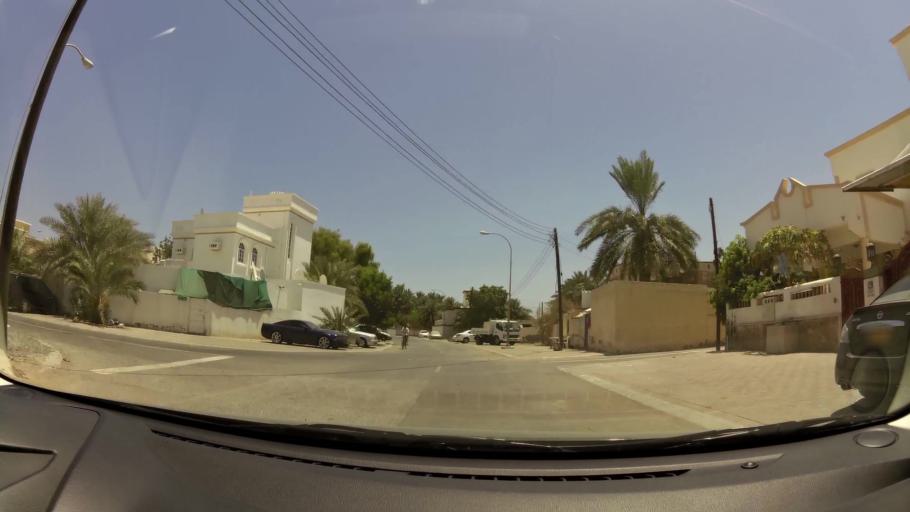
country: OM
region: Muhafazat Masqat
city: As Sib al Jadidah
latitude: 23.6246
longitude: 58.2440
